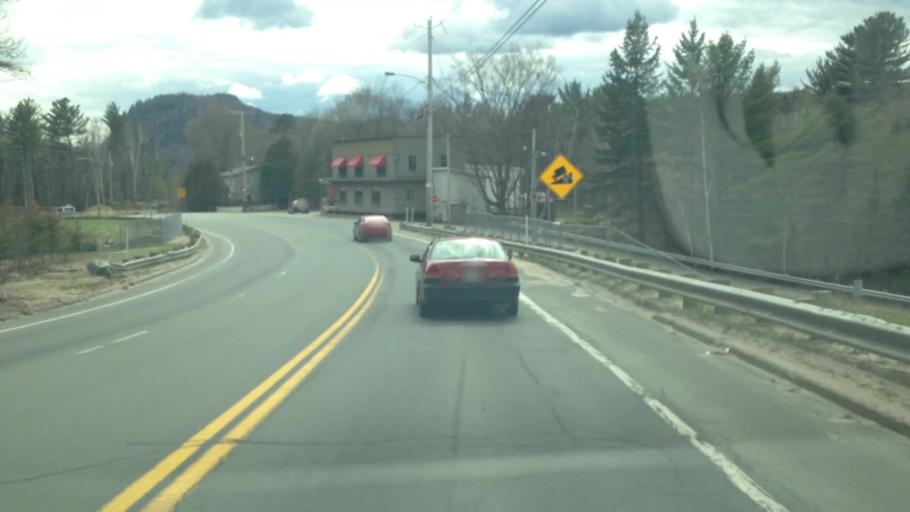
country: CA
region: Quebec
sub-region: Laurentides
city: Sainte-Adele
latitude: 45.9899
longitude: -74.1175
